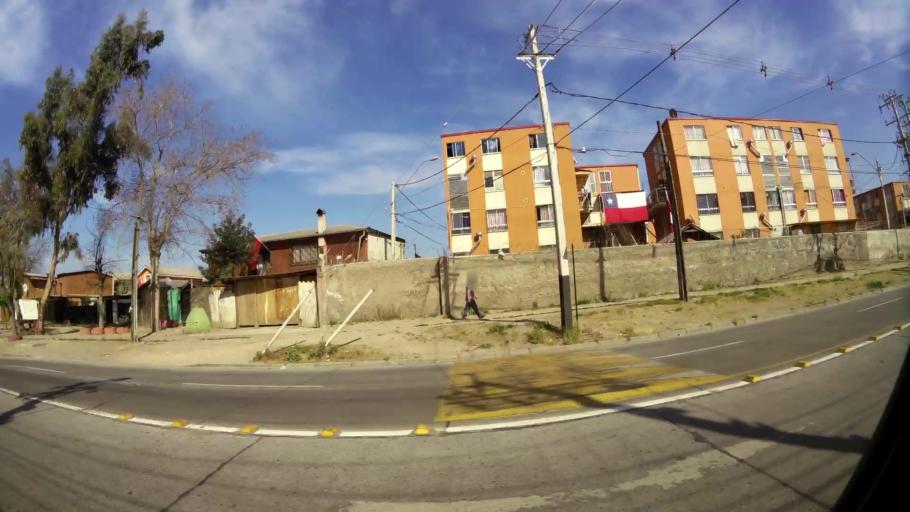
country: CL
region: Santiago Metropolitan
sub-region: Provincia de Santiago
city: Lo Prado
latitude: -33.4440
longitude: -70.7638
